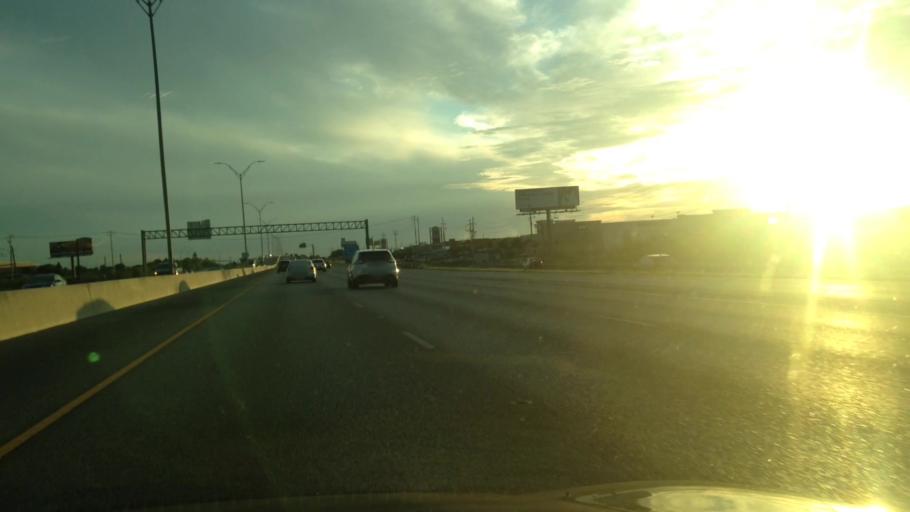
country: US
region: Texas
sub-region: Hays County
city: San Marcos
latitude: 29.8458
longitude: -97.9656
